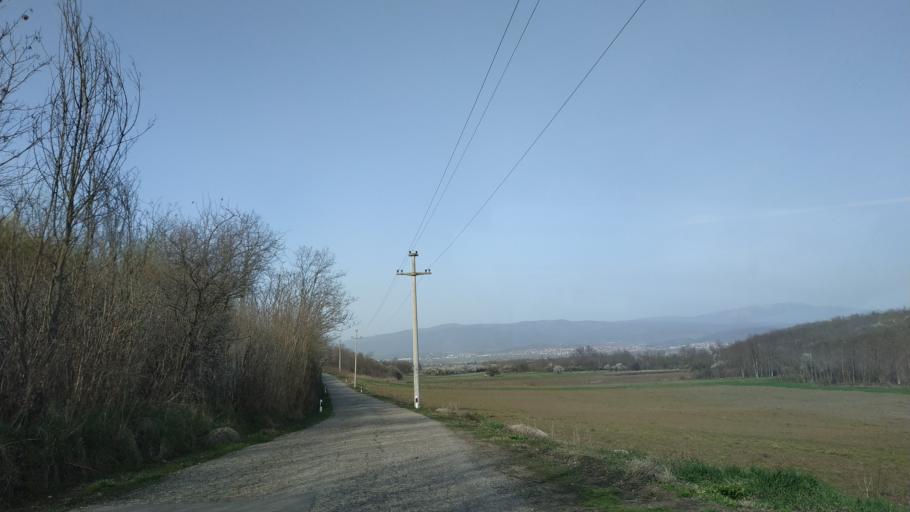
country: RS
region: Central Serbia
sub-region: Nisavski Okrug
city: Aleksinac
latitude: 43.5101
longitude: 21.6460
